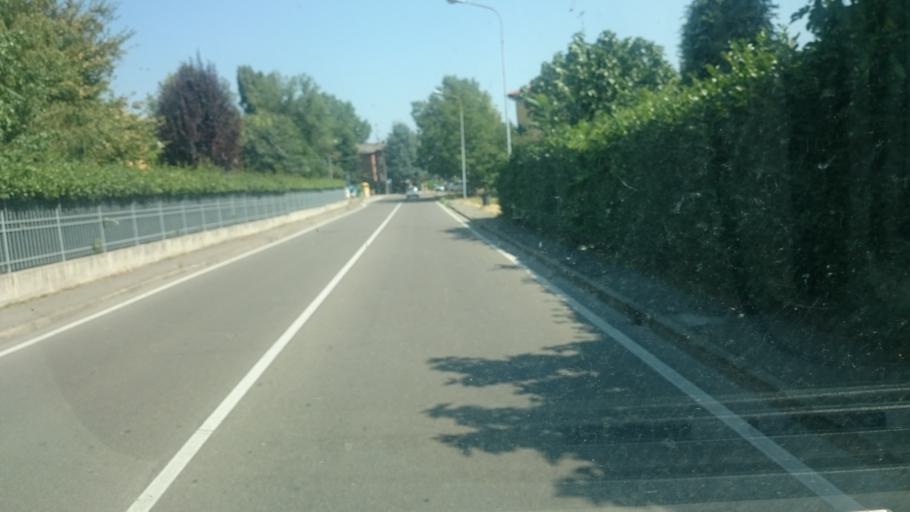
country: IT
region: Emilia-Romagna
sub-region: Provincia di Reggio Emilia
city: Scandiano
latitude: 44.6044
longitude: 10.6901
